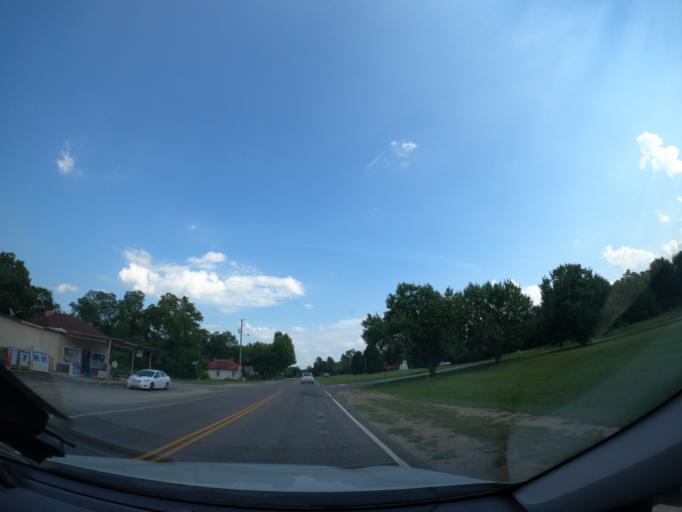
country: US
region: South Carolina
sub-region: Barnwell County
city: Williston
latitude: 33.4817
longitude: -81.5134
